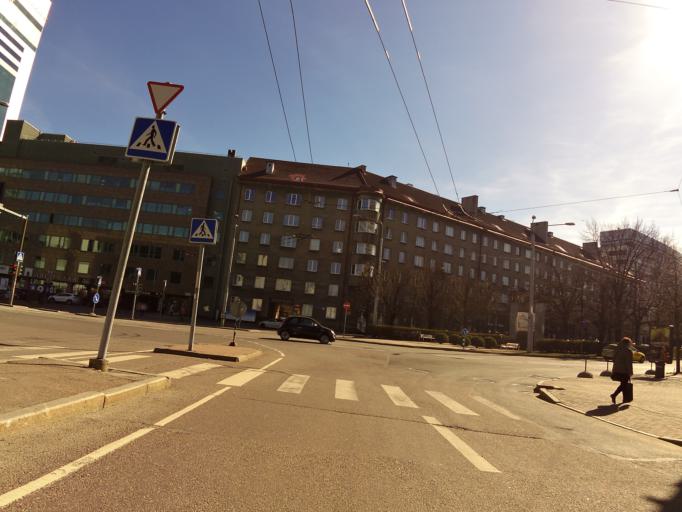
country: EE
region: Harju
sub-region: Tallinna linn
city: Tallinn
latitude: 59.4341
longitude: 24.7559
